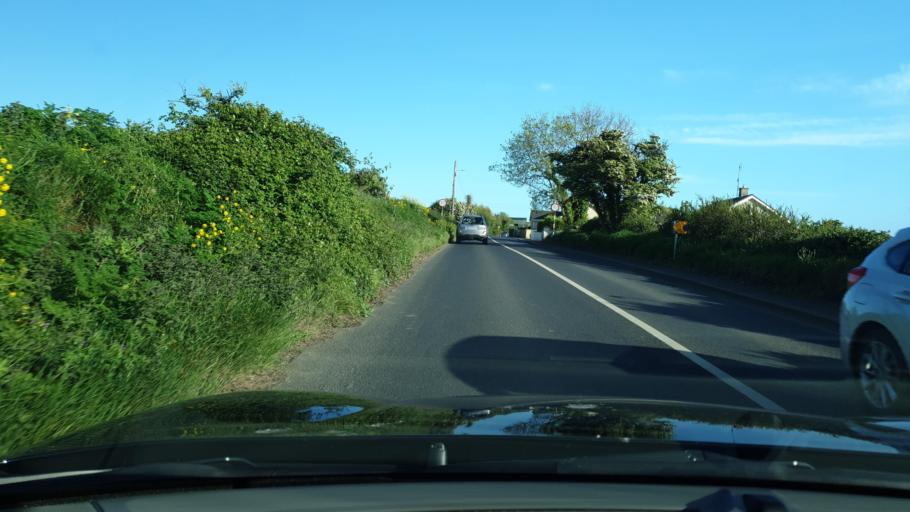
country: IE
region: Leinster
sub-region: Fingal County
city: Skerries
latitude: 53.5601
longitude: -6.1036
